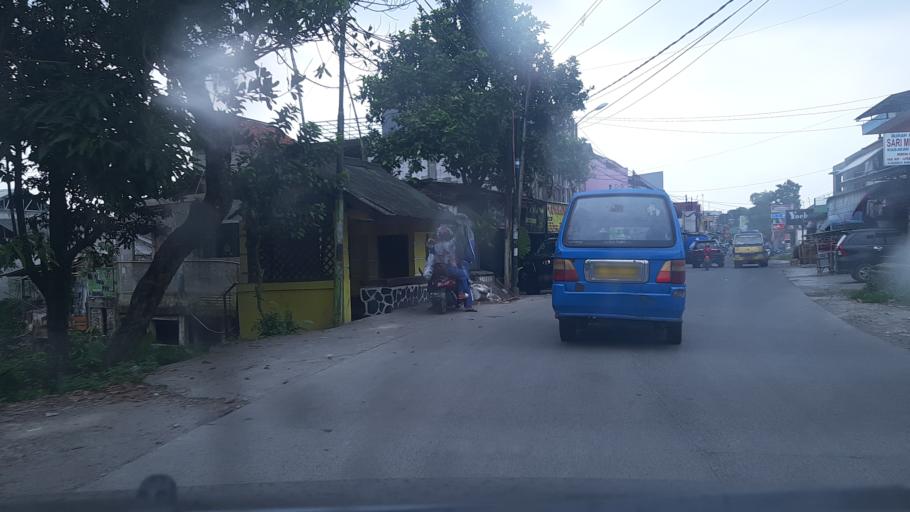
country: ID
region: West Java
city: Bogor
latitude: -6.5662
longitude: 106.8640
